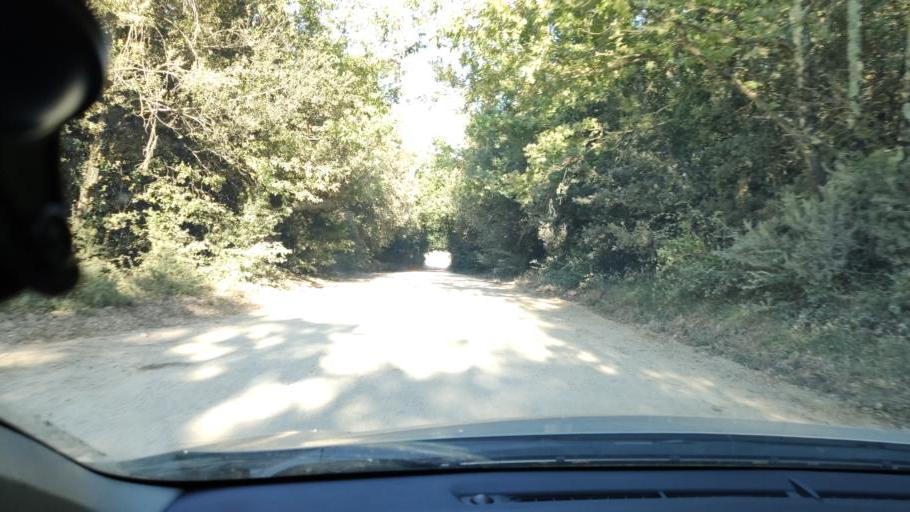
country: IT
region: Umbria
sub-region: Provincia di Terni
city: Penna in Teverina
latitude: 42.5397
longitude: 12.3697
